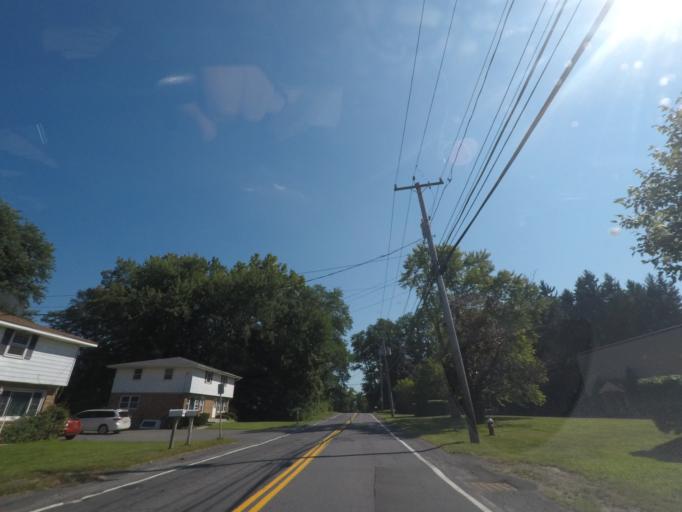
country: US
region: New York
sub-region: Albany County
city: Colonie
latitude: 42.7414
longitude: -73.7922
